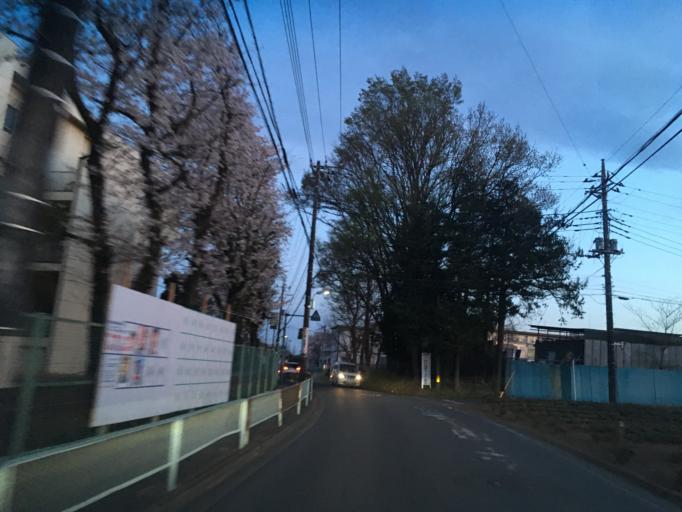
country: JP
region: Saitama
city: Sayama
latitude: 35.8036
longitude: 139.4017
